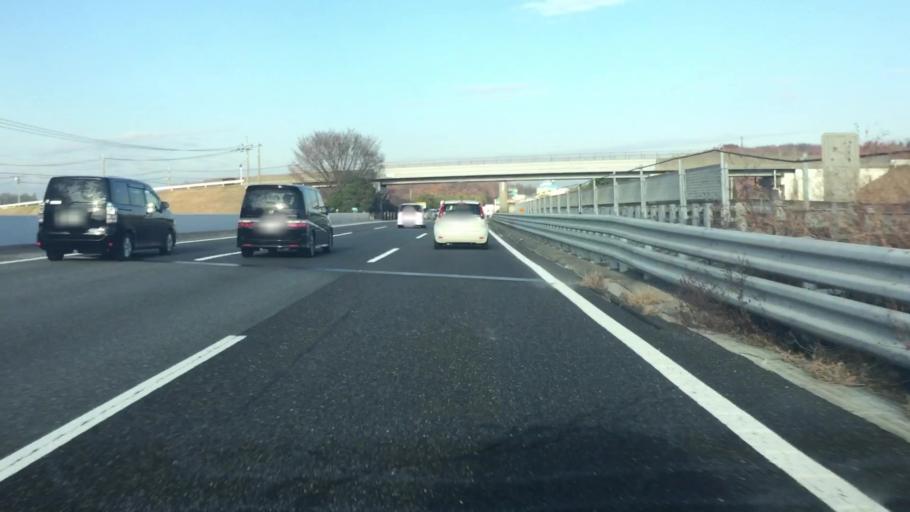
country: JP
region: Saitama
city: Honjo
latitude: 36.2056
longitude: 139.1744
